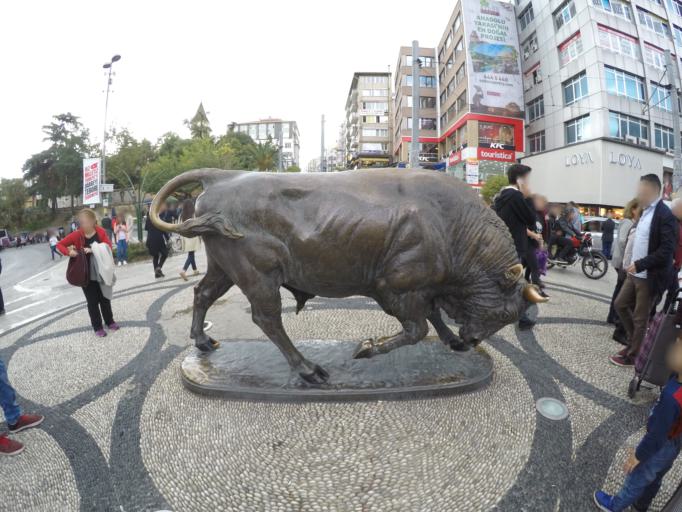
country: TR
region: Istanbul
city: UEskuedar
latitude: 40.9905
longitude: 29.0290
